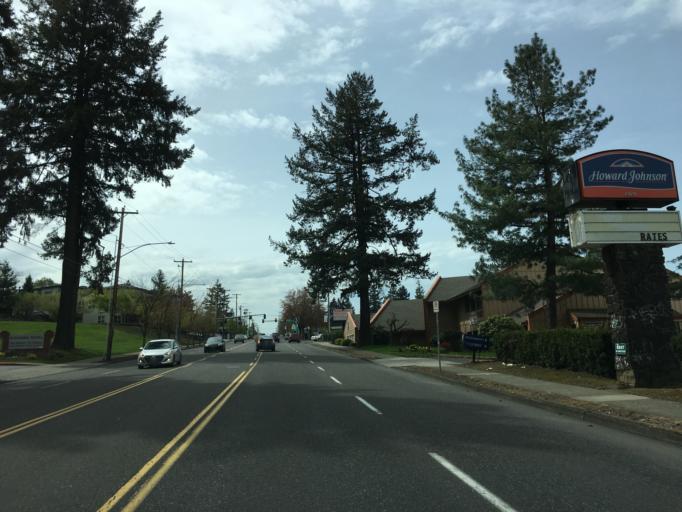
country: US
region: Oregon
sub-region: Multnomah County
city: Lents
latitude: 45.5533
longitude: -122.5767
